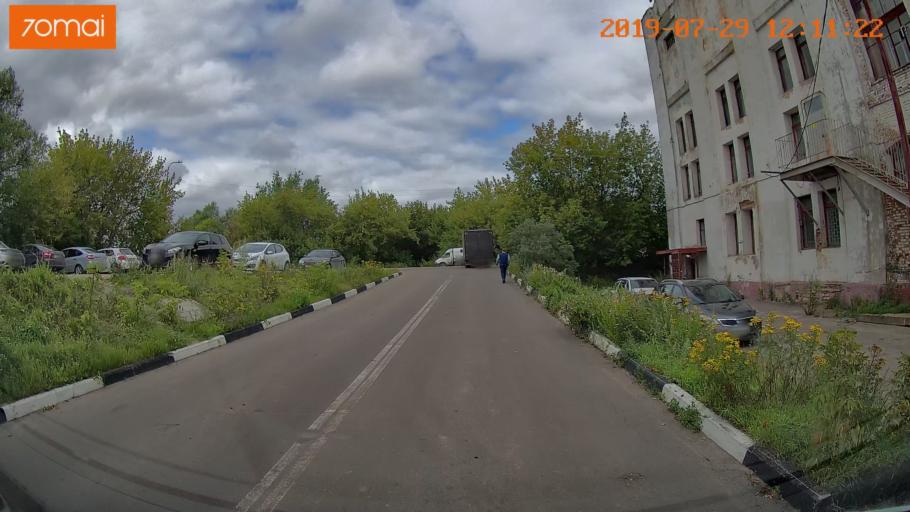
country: RU
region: Ivanovo
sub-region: Gorod Ivanovo
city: Ivanovo
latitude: 57.0095
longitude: 40.9645
